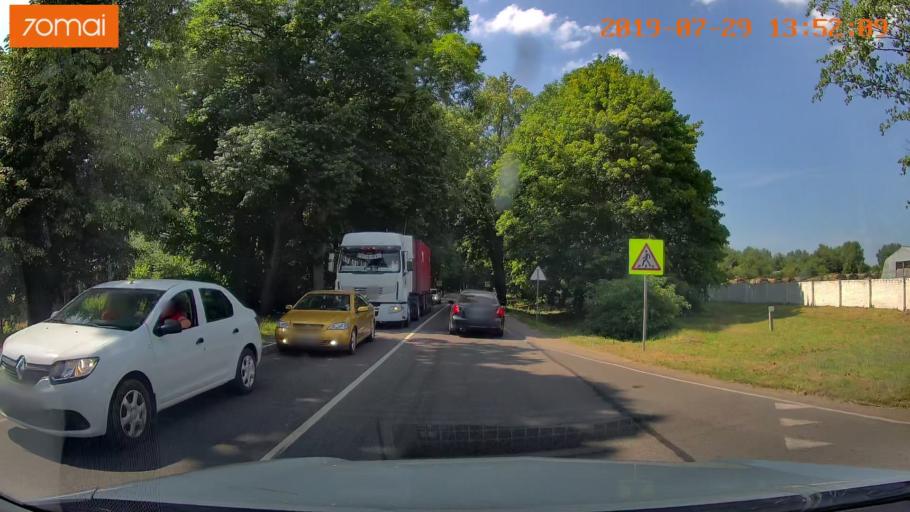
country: RU
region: Kaliningrad
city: Primorsk
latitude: 54.7298
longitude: 19.9979
